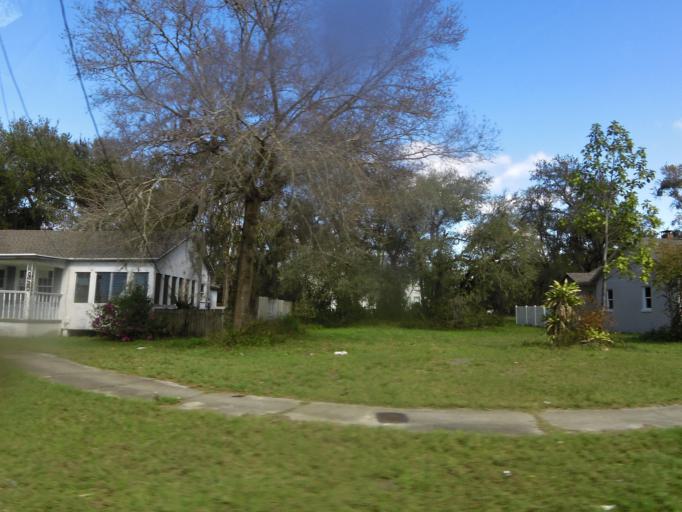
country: US
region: Florida
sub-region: Seminole County
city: Sanford
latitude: 28.8014
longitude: -81.2624
